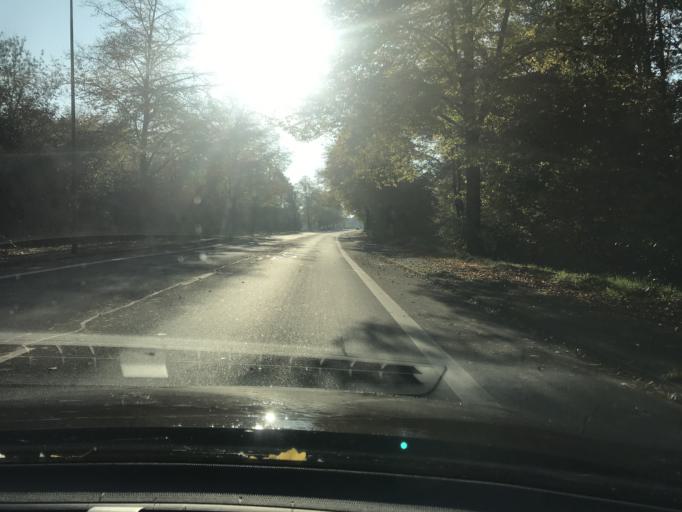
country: DE
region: North Rhine-Westphalia
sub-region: Regierungsbezirk Arnsberg
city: Hamm
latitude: 51.6824
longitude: 7.8512
